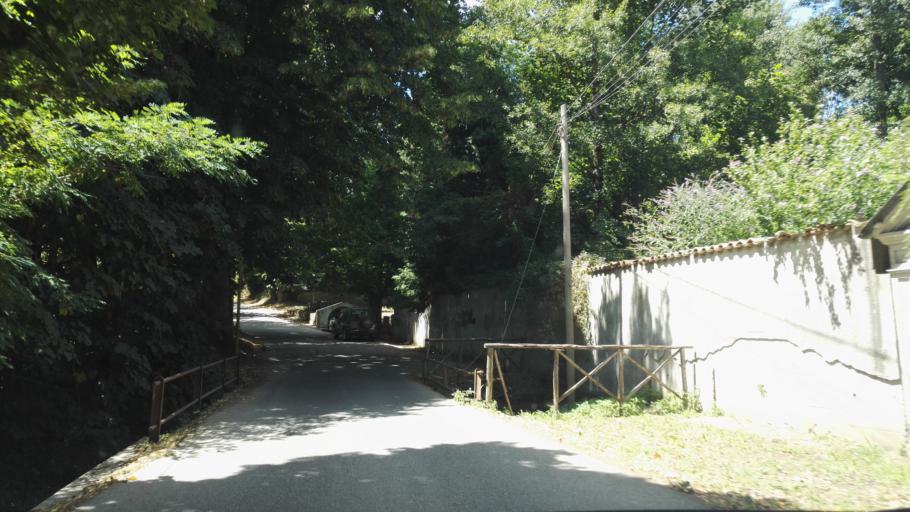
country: IT
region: Calabria
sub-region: Provincia di Vibo-Valentia
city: Serra San Bruno
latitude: 38.5790
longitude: 16.3236
